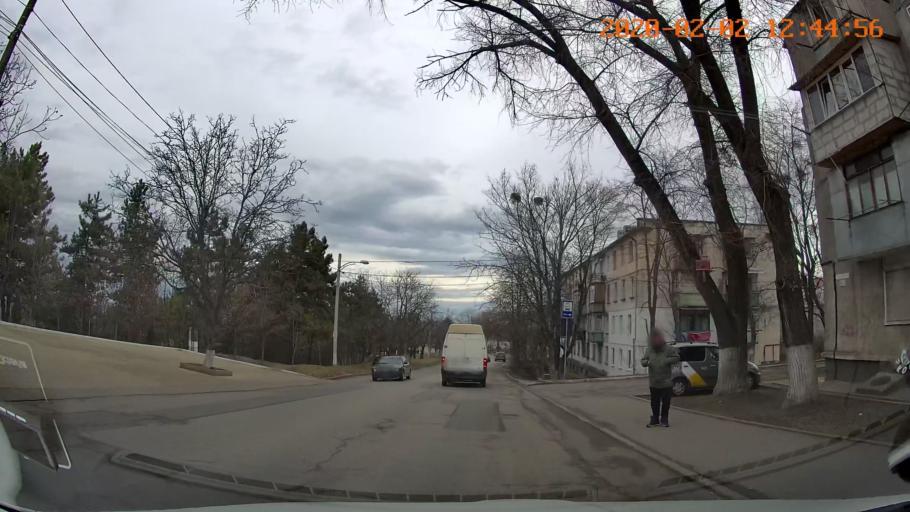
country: MD
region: Chisinau
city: Chisinau
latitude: 47.0043
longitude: 28.8106
